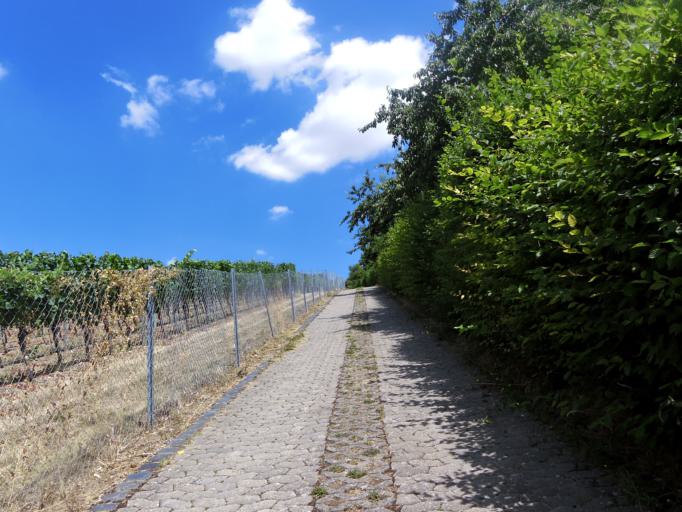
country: DE
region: Bavaria
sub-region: Regierungsbezirk Unterfranken
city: Wuerzburg
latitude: 49.8057
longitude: 9.9510
